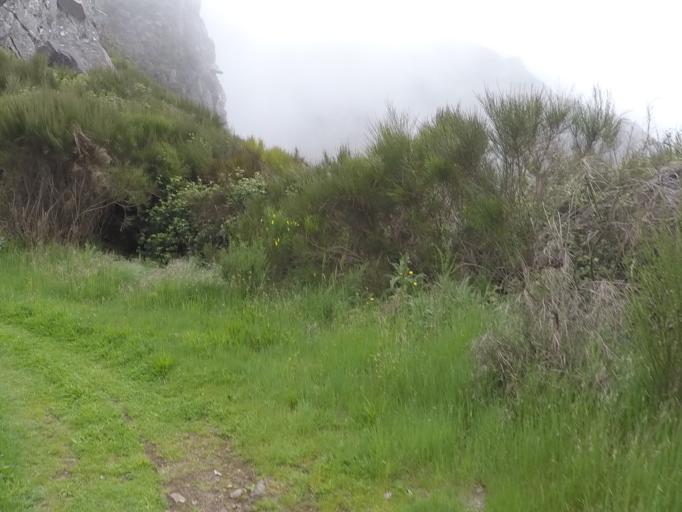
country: PT
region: Madeira
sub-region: Camara de Lobos
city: Curral das Freiras
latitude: 32.7184
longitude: -16.9903
